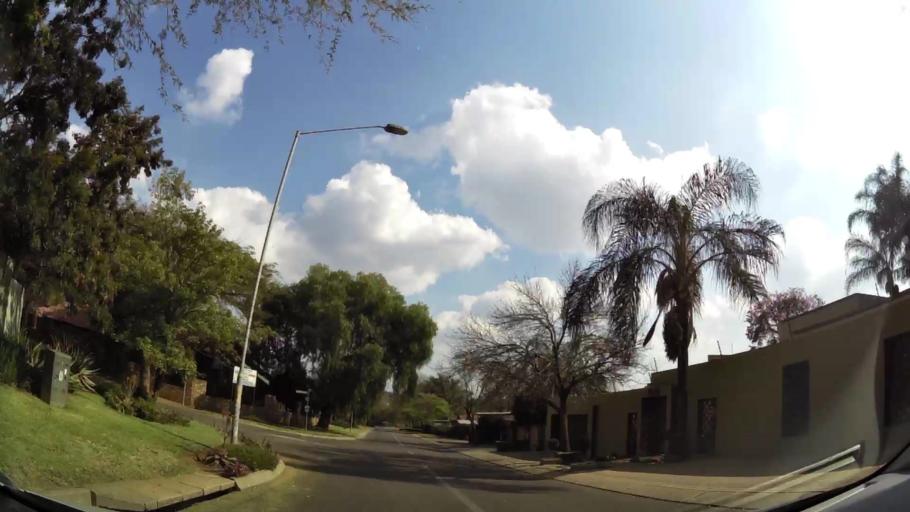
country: ZA
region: Gauteng
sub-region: City of Tshwane Metropolitan Municipality
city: Pretoria
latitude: -25.7949
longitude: 28.3268
